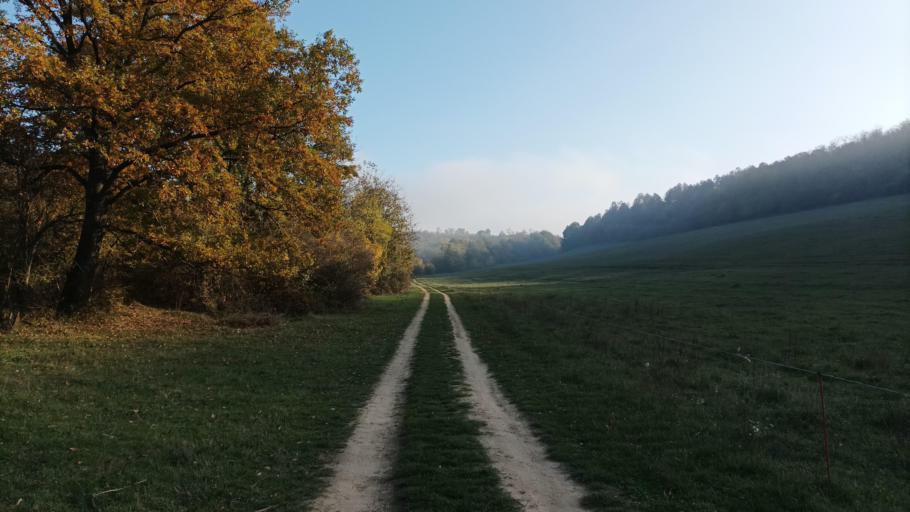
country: HU
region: Tolna
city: Szentgalpuszta
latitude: 46.3266
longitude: 18.6079
